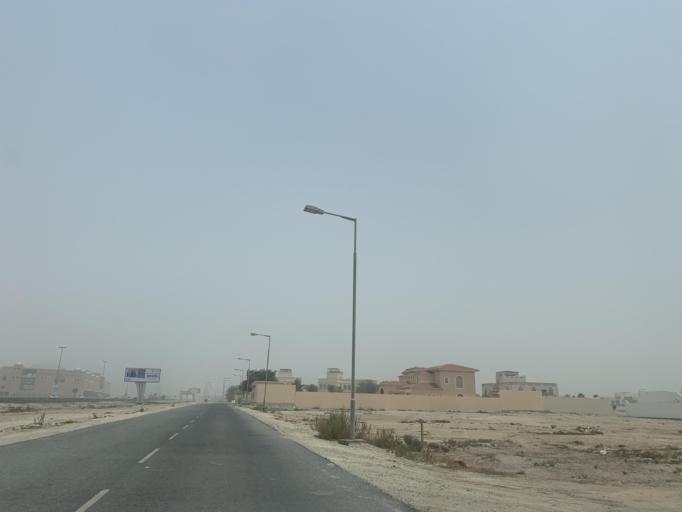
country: BH
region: Central Governorate
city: Madinat Hamad
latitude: 26.1725
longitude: 50.4721
